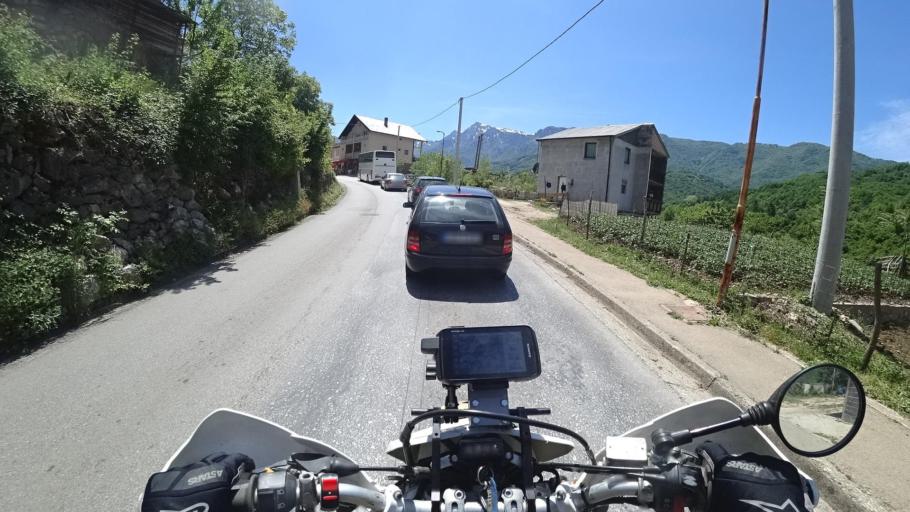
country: BA
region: Federation of Bosnia and Herzegovina
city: Polje-Bijela
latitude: 43.6257
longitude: 17.9678
